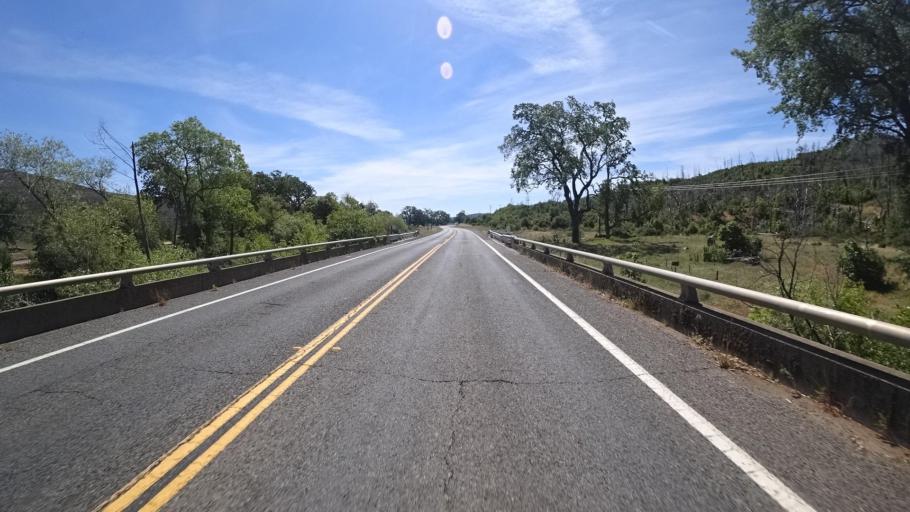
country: US
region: California
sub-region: Lake County
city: Middletown
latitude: 38.7726
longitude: -122.6656
